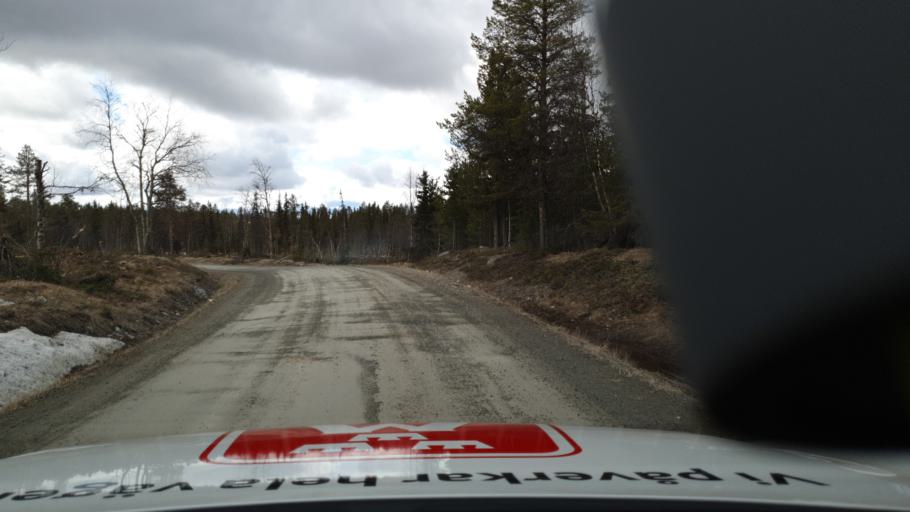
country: SE
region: Jaemtland
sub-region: Are Kommun
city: Jarpen
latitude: 62.8224
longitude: 13.8102
